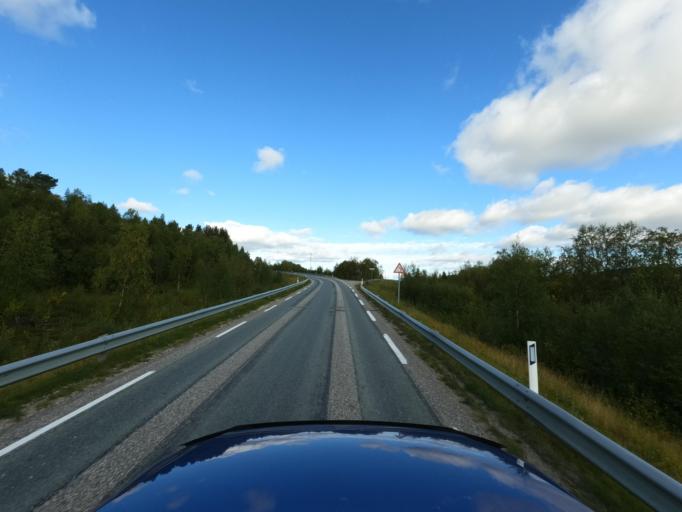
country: NO
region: Finnmark Fylke
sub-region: Karasjok
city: Karasjohka
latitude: 69.4276
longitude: 25.7942
